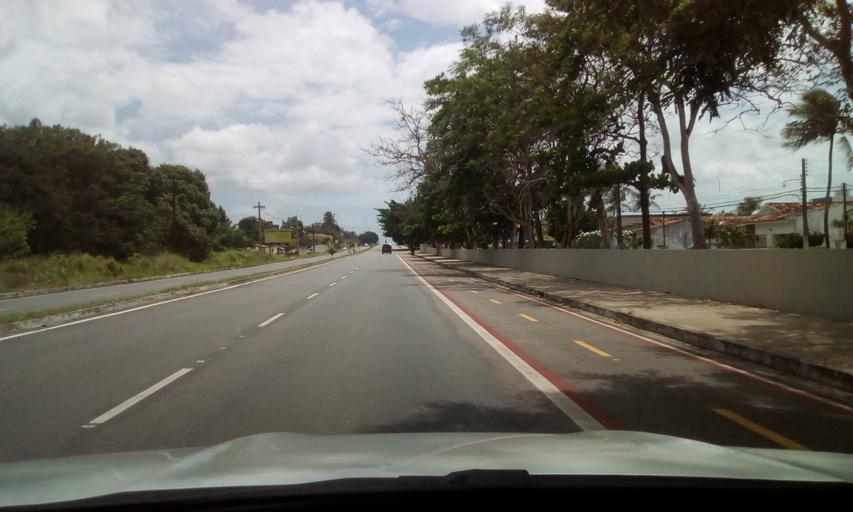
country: BR
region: Paraiba
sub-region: Bayeux
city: Bayeux
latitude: -7.1372
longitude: -34.9418
